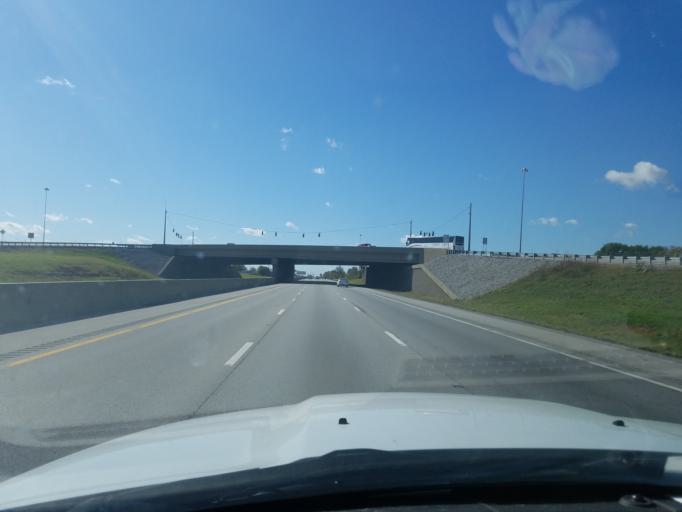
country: US
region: Kentucky
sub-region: Warren County
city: Plano
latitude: 36.9361
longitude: -86.4174
